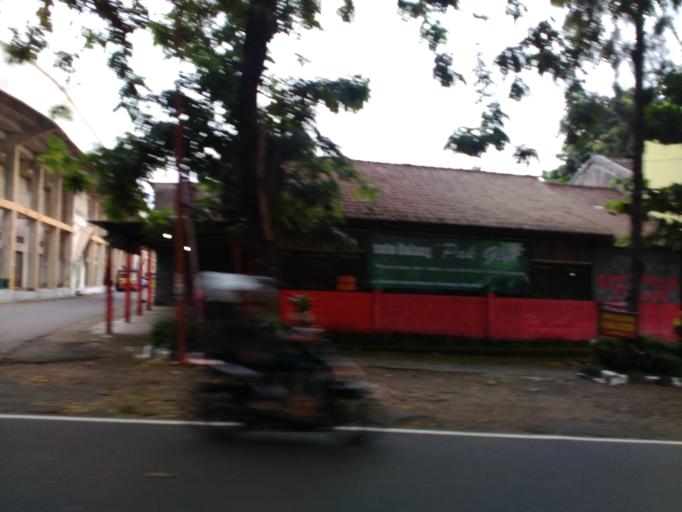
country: ID
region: Central Java
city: Boyolali
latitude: -7.5451
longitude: 110.6033
